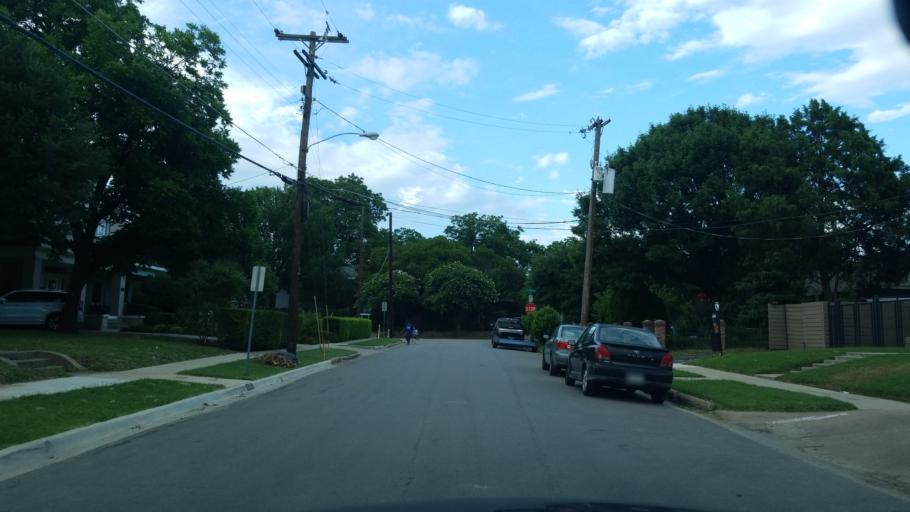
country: US
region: Texas
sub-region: Dallas County
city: Highland Park
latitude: 32.8063
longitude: -96.7790
